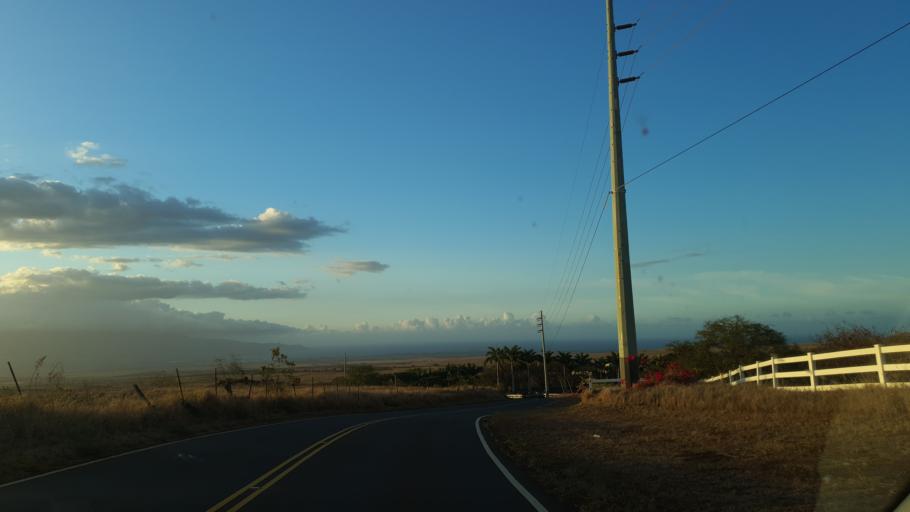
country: US
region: Hawaii
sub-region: Maui County
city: Pukalani
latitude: 20.7980
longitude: -156.3717
